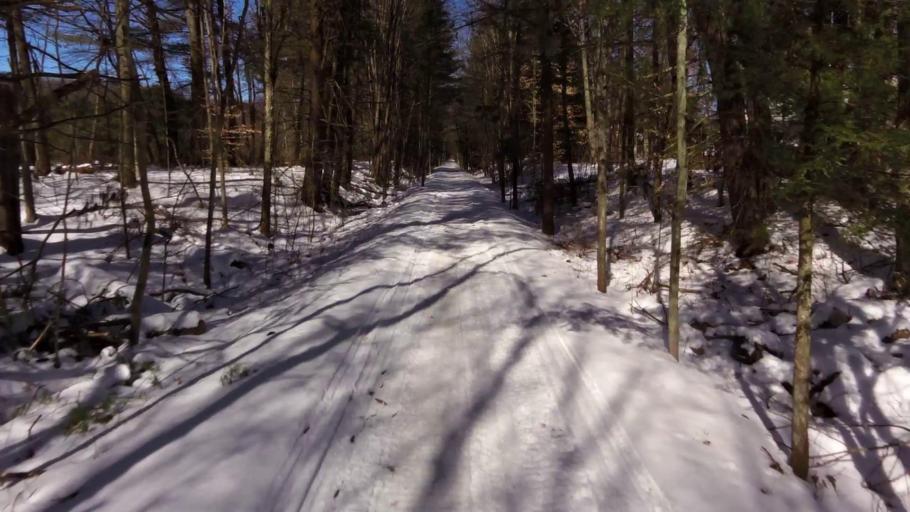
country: US
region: New York
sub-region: Allegany County
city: Houghton
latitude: 42.3568
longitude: -78.1291
